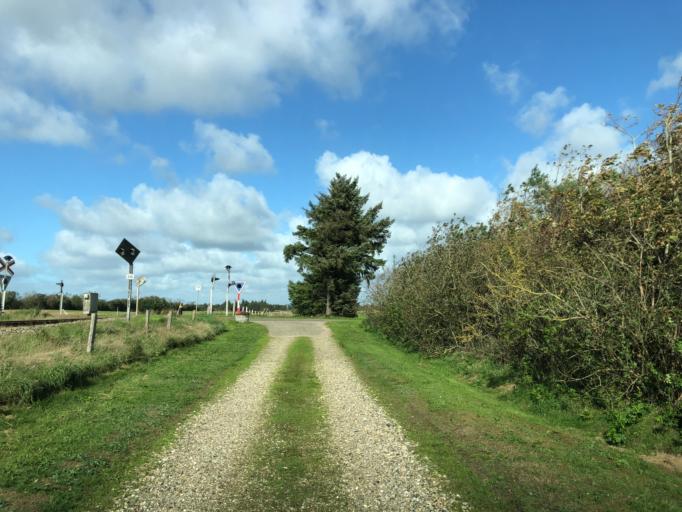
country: DK
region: Central Jutland
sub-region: Holstebro Kommune
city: Ulfborg
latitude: 56.2884
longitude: 8.3295
